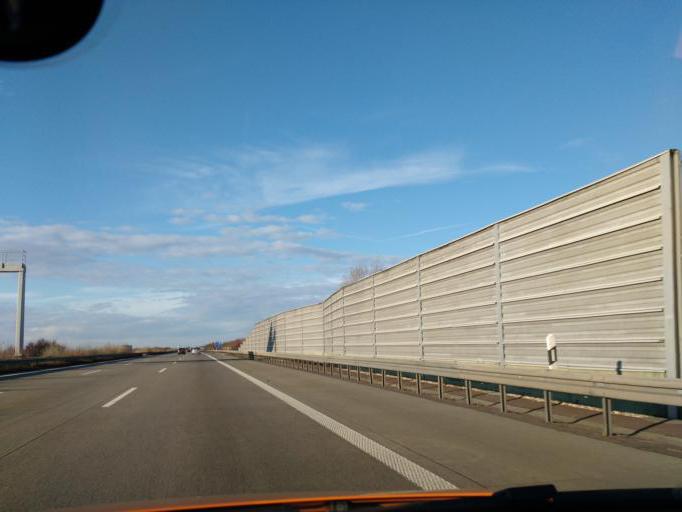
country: DE
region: Saxony-Anhalt
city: Erxleben
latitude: 52.1980
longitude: 11.2558
